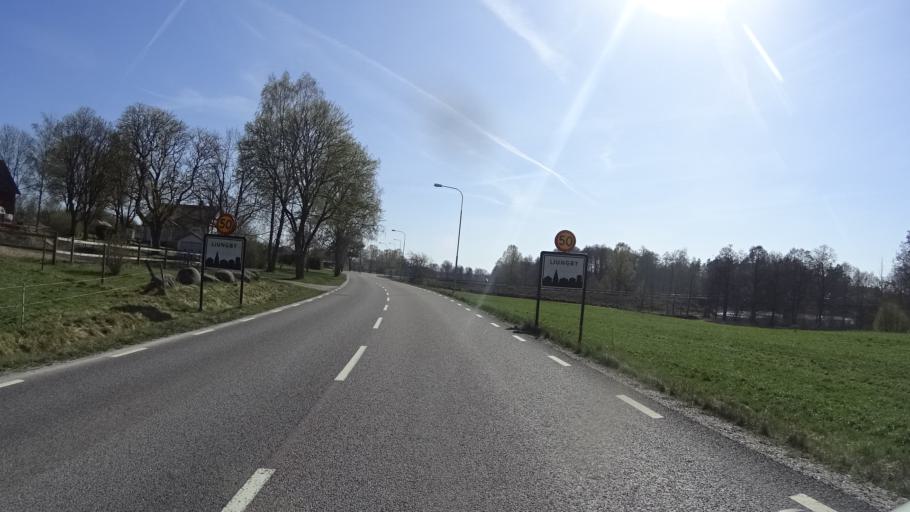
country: SE
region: Kronoberg
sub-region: Ljungby Kommun
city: Ljungby
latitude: 56.8440
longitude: 13.9718
